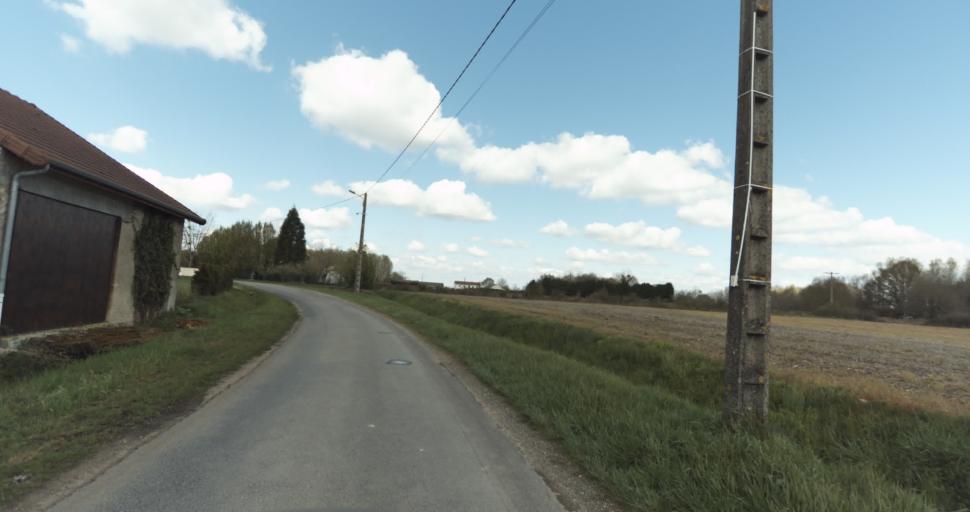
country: FR
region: Bourgogne
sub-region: Departement de la Cote-d'Or
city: Auxonne
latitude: 47.2142
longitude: 5.4297
